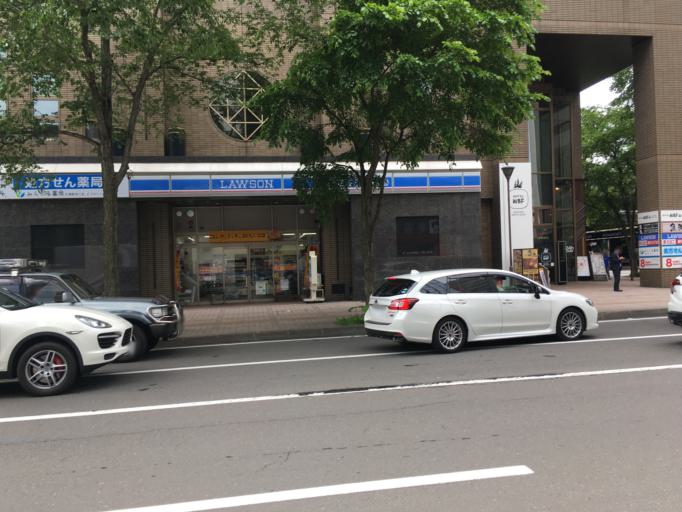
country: JP
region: Hokkaido
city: Sapporo
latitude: 43.0689
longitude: 141.3488
